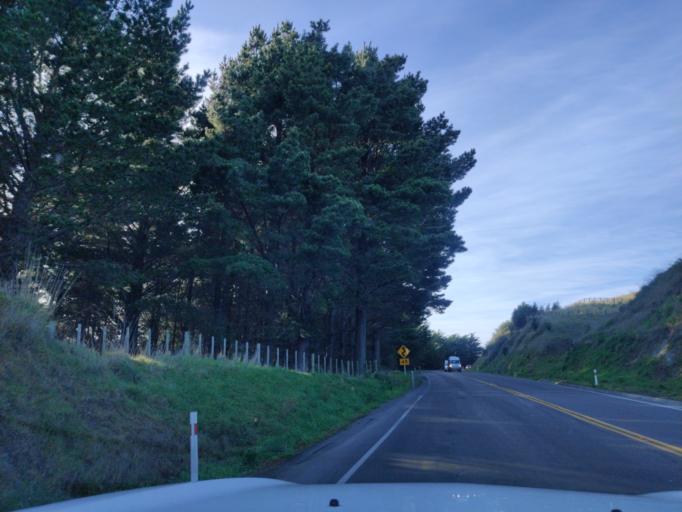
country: NZ
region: Manawatu-Wanganui
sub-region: Palmerston North City
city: Palmerston North
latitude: -40.2856
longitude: 175.7904
